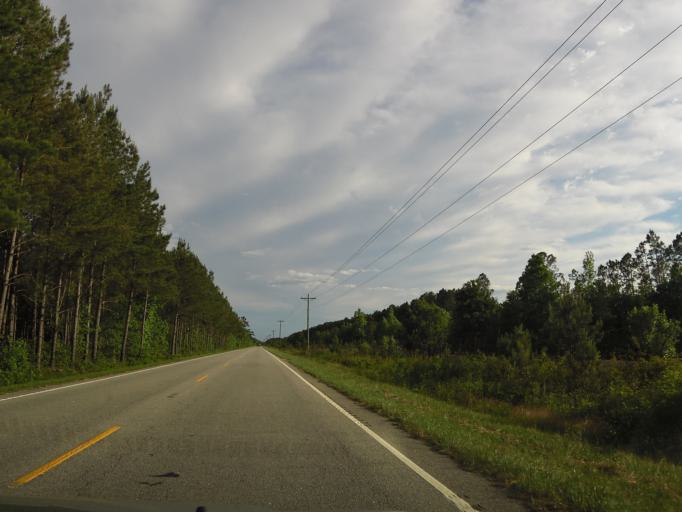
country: US
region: South Carolina
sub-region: Hampton County
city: Estill
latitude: 32.6355
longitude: -81.2442
